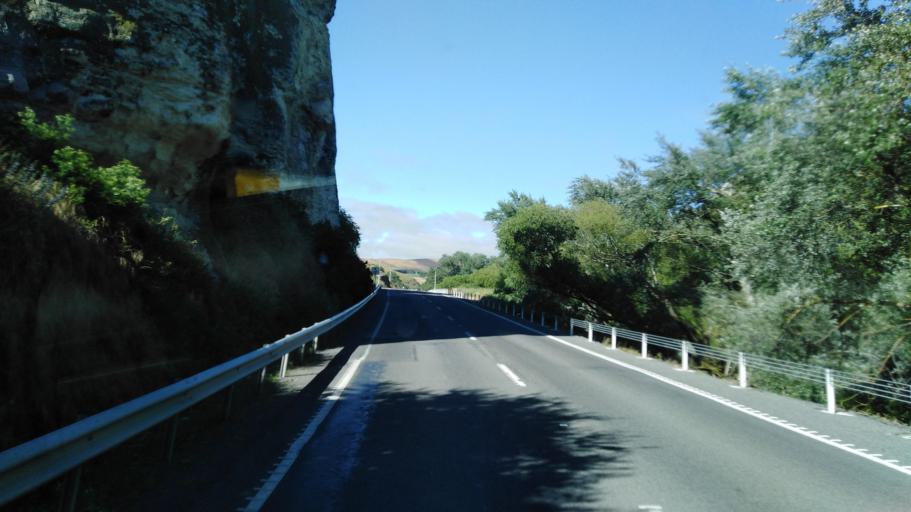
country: NZ
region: Canterbury
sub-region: Hurunui District
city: Amberley
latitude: -42.9995
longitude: 172.7144
